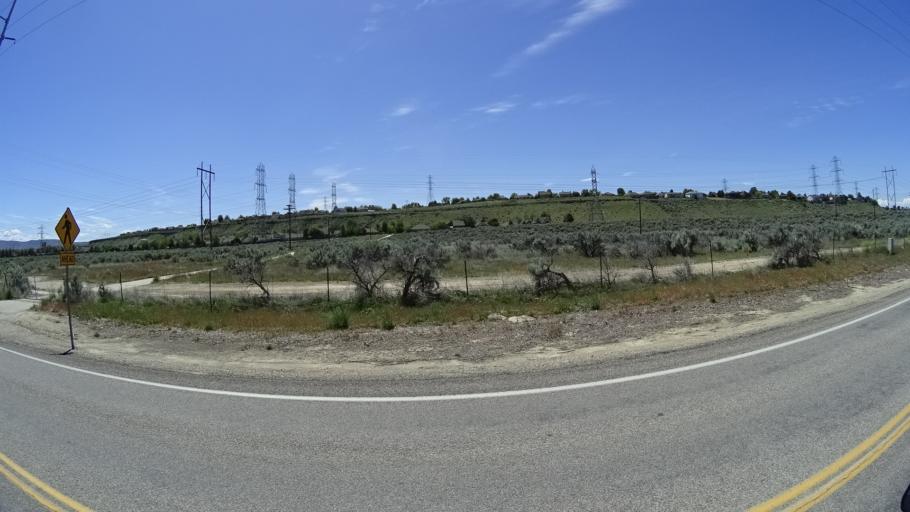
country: US
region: Idaho
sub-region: Ada County
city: Boise
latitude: 43.5606
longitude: -116.1344
